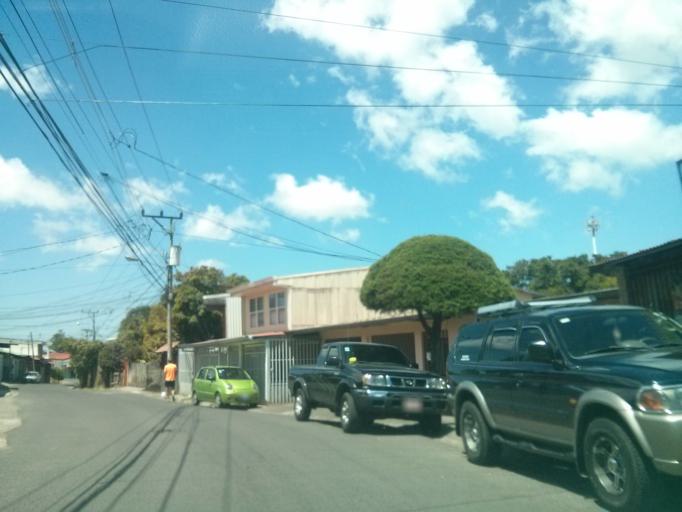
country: CR
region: San Jose
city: San Miguel
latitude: 9.8887
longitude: -84.0625
